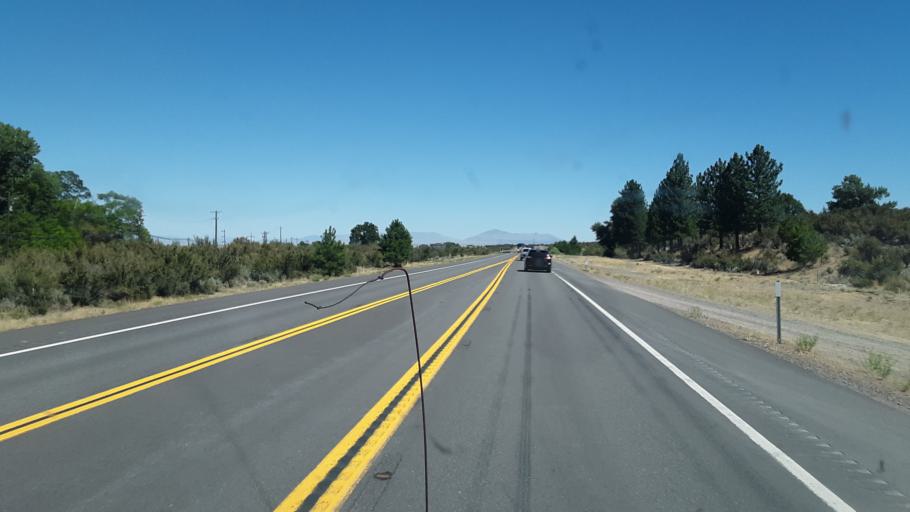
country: US
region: California
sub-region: Lassen County
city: Janesville
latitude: 40.2897
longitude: -120.4998
